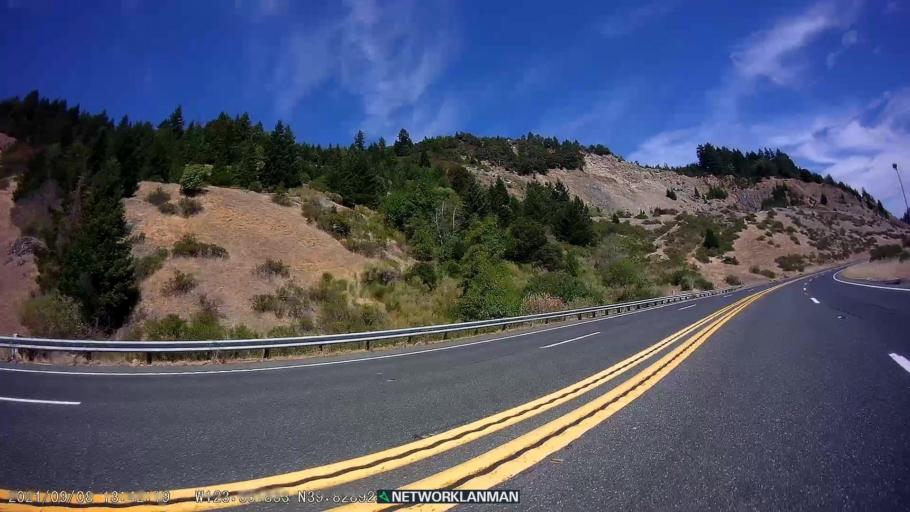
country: US
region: California
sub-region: Mendocino County
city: Laytonville
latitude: 39.8302
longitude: -123.6630
